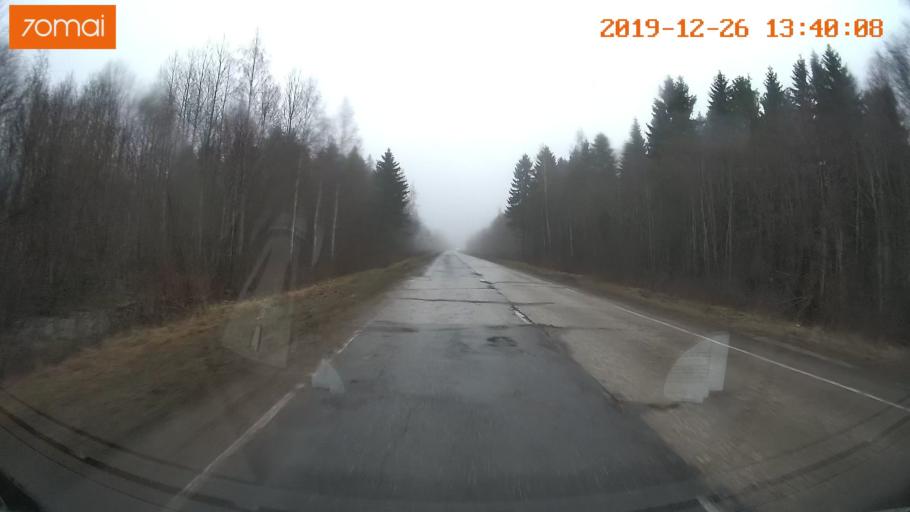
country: RU
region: Vologda
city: Sheksna
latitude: 58.7455
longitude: 38.4239
